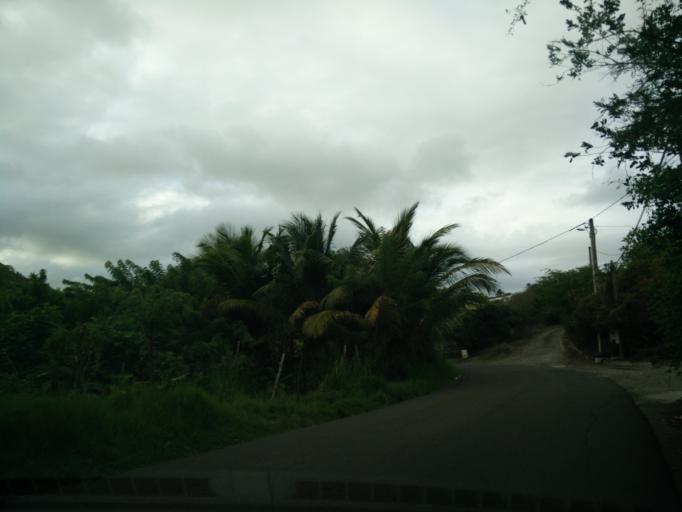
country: MQ
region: Martinique
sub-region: Martinique
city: Le Marin
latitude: 14.4454
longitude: -60.8361
